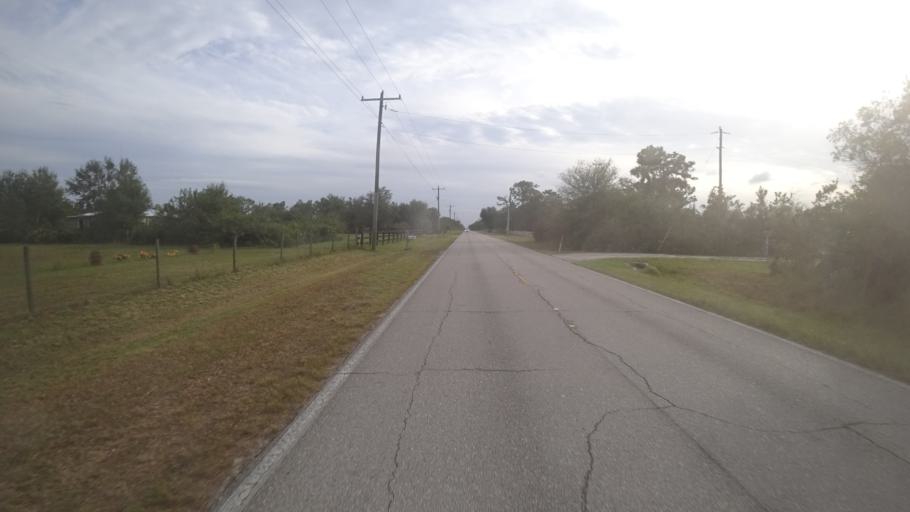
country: US
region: Florida
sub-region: Sarasota County
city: The Meadows
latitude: 27.4250
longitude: -82.2708
